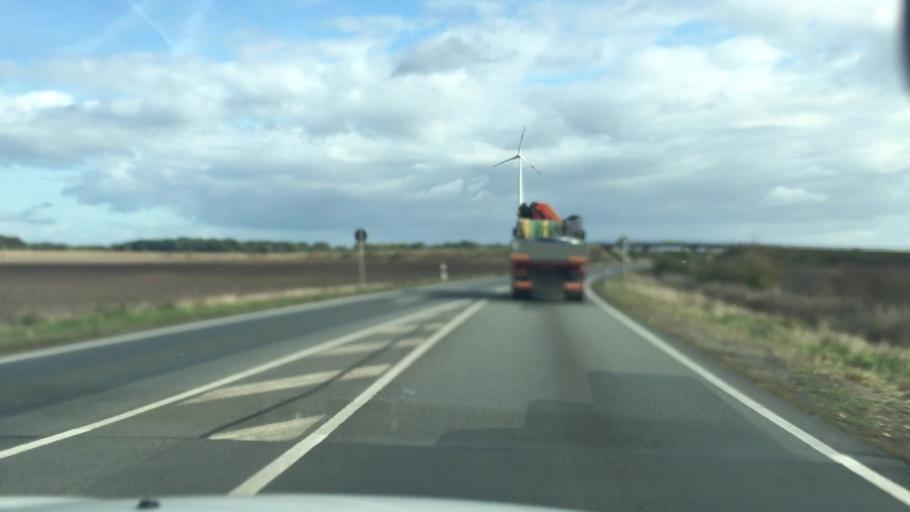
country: DE
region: Lower Saxony
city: Diepholz
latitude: 52.6276
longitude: 8.4014
